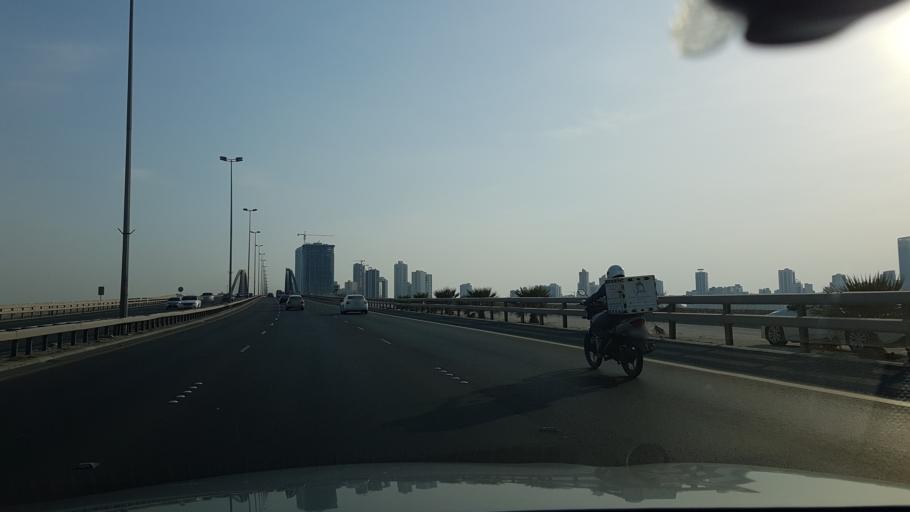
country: BH
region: Muharraq
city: Al Hadd
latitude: 26.2232
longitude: 50.6313
